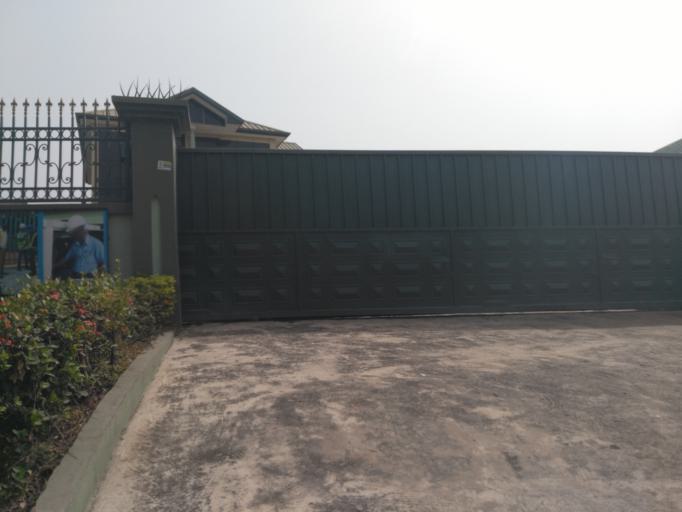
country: GH
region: Ashanti
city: Kumasi
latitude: 6.6788
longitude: -1.6013
